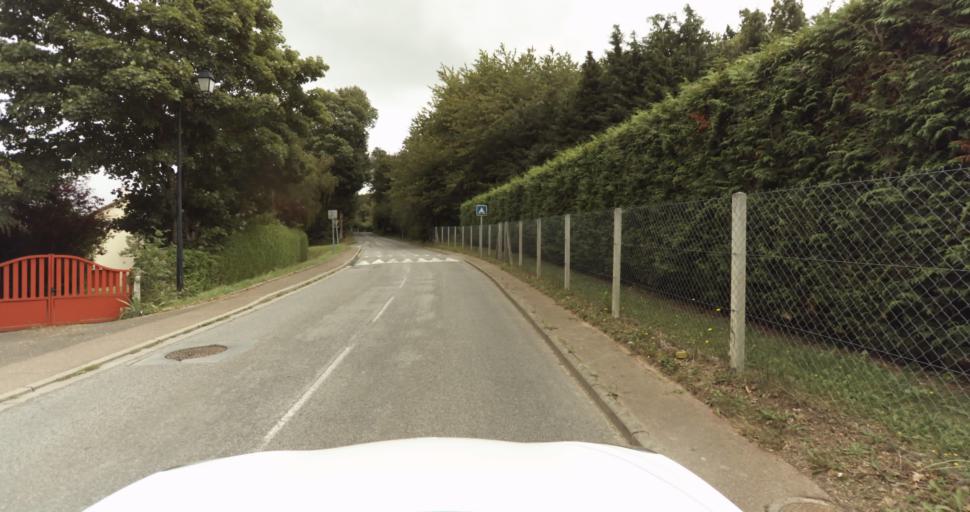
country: FR
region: Haute-Normandie
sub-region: Departement de l'Eure
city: Saint-Sebastien-de-Morsent
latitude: 48.9912
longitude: 1.0527
